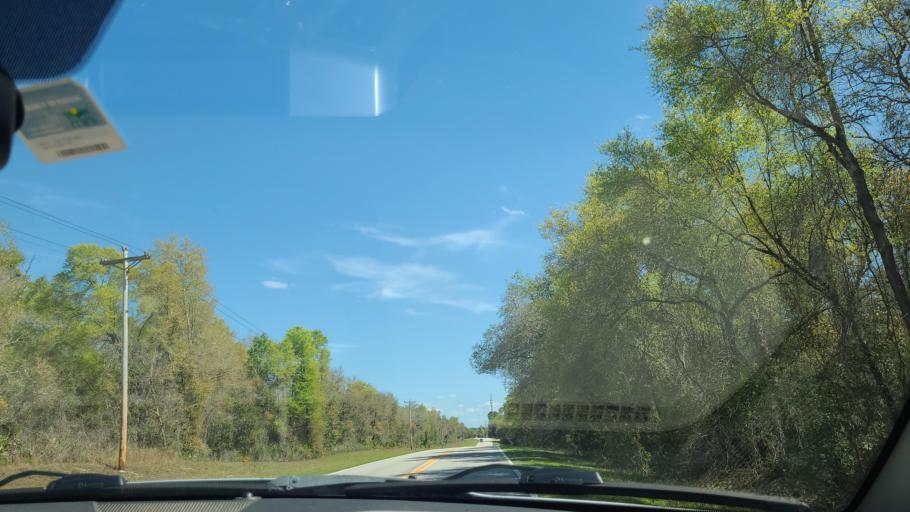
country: US
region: Florida
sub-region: Putnam County
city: Crescent City
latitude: 29.3773
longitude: -81.7541
